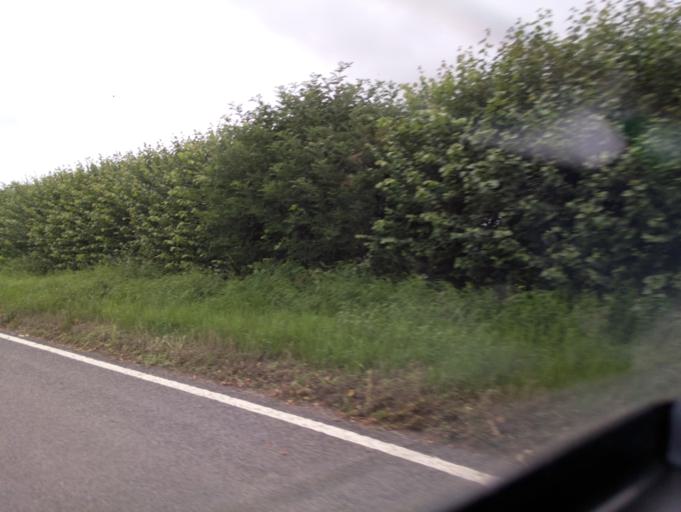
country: GB
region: England
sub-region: Worcestershire
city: Upton upon Severn
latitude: 52.0997
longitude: -2.2118
